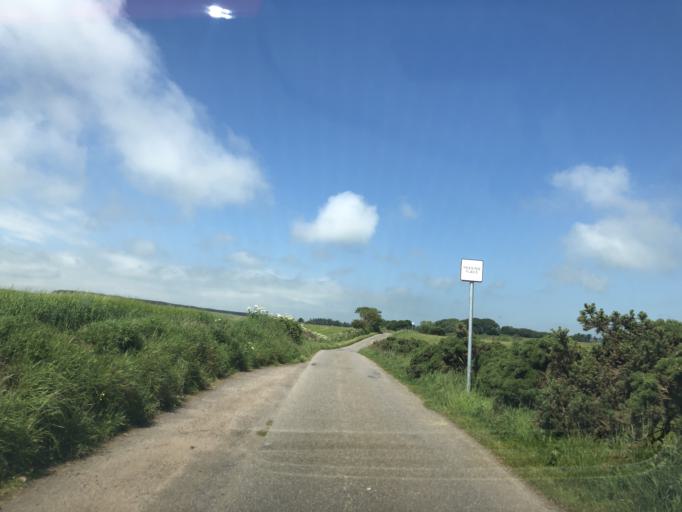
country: GB
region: Scotland
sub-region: Aberdeenshire
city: Stonehaven
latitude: 56.9134
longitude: -2.2021
